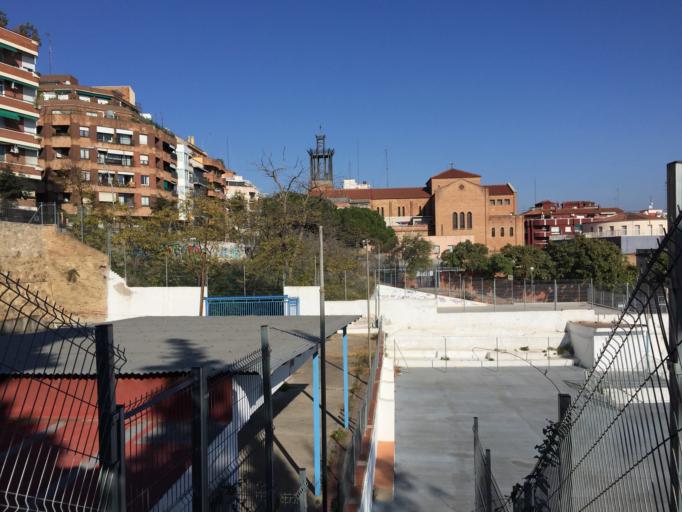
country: ES
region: Catalonia
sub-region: Provincia de Barcelona
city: Horta-Guinardo
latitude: 41.4165
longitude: 2.1710
